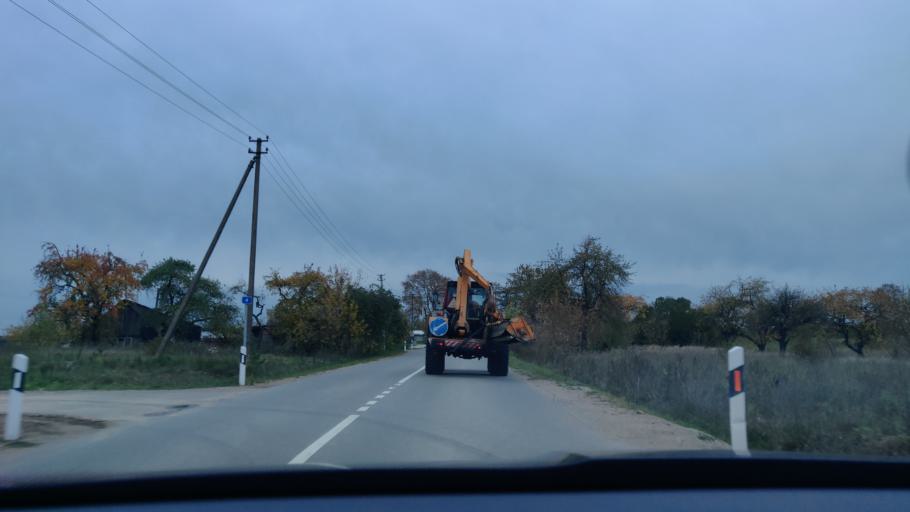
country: LT
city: Lentvaris
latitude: 54.6002
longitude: 25.0193
